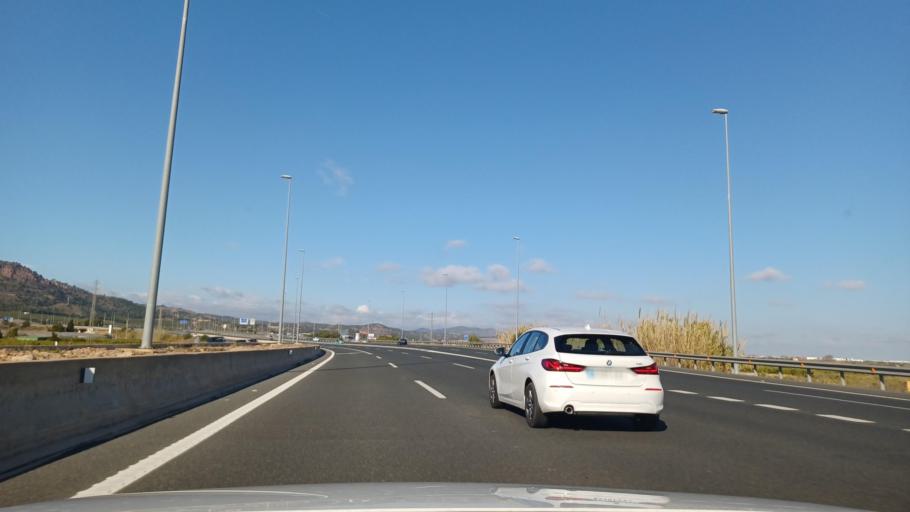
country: ES
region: Valencia
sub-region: Provincia de Valencia
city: Pucol
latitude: 39.6220
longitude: -0.2950
